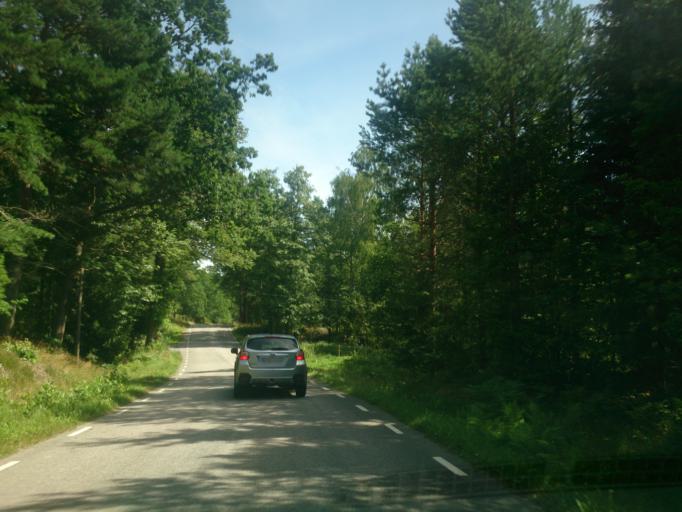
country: SE
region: OEstergoetland
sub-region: Valdemarsviks Kommun
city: Valdemarsvik
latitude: 58.2722
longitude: 16.7176
